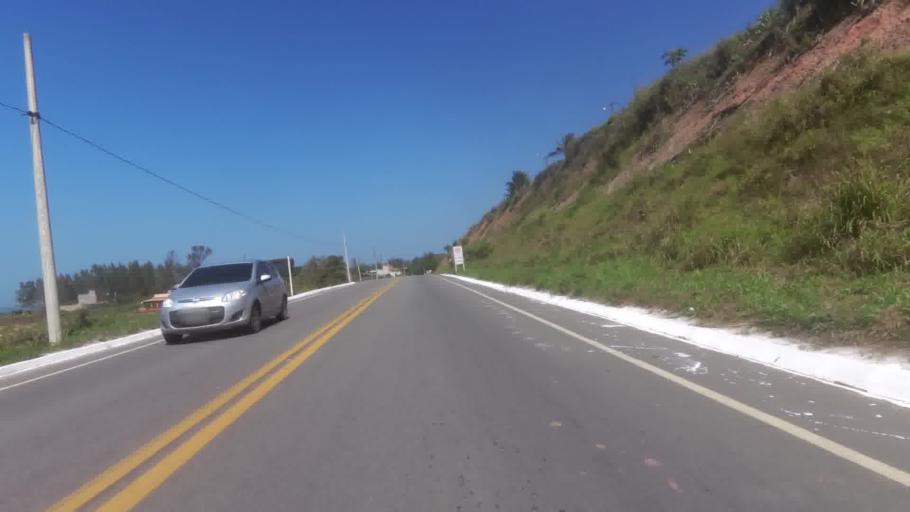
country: BR
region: Espirito Santo
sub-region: Marataizes
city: Marataizes
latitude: -21.1095
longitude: -40.8545
